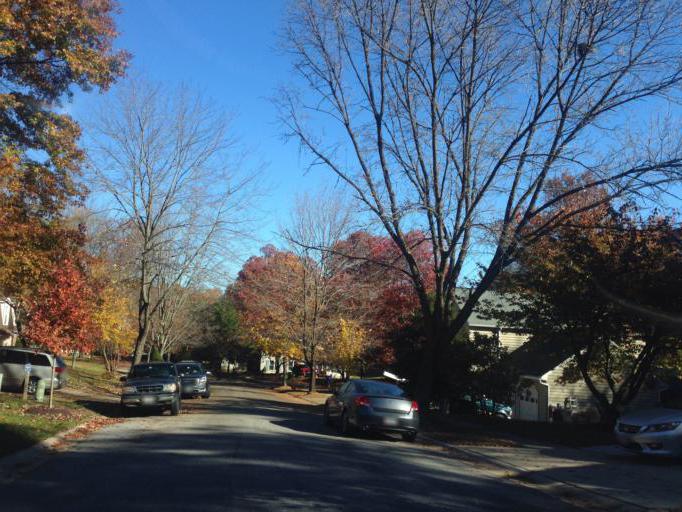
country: US
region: Maryland
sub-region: Howard County
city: Riverside
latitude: 39.2037
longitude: -76.8667
